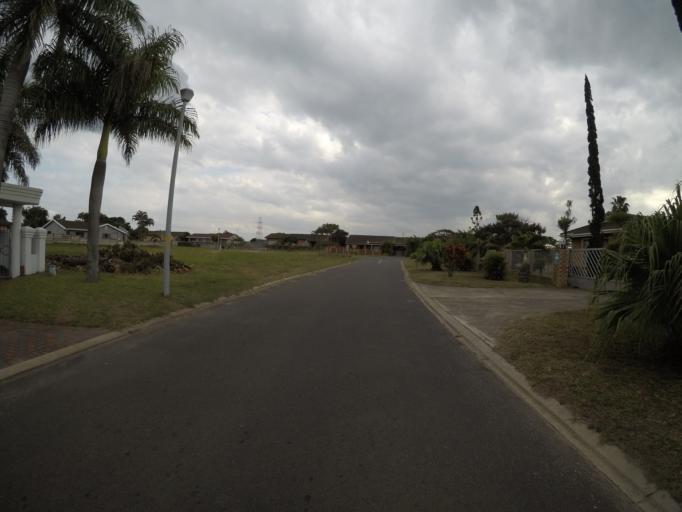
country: ZA
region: KwaZulu-Natal
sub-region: uThungulu District Municipality
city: Richards Bay
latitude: -28.7351
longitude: 32.0445
